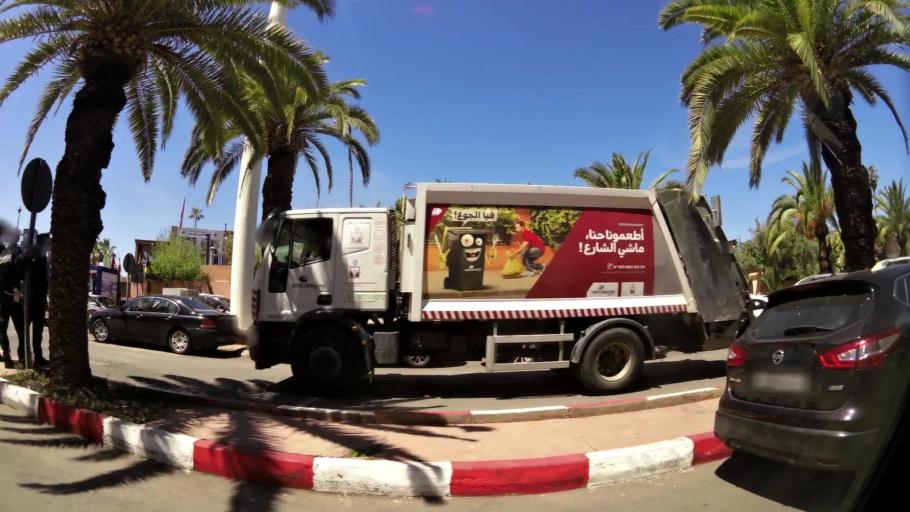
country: MA
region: Marrakech-Tensift-Al Haouz
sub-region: Marrakech
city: Marrakesh
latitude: 31.6296
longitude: -8.0083
